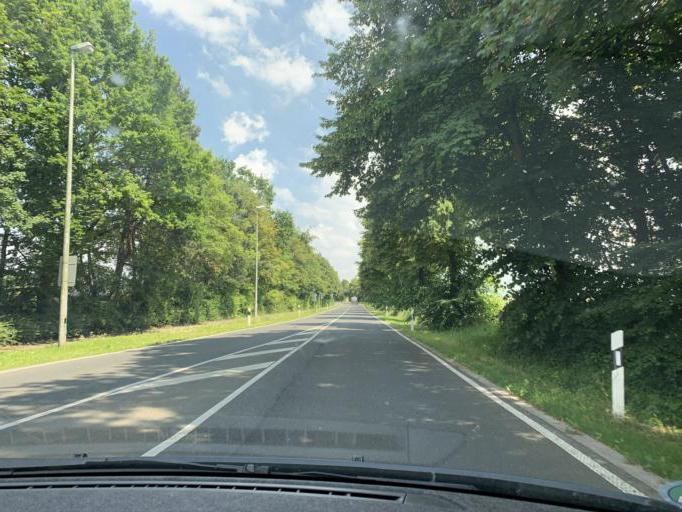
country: DE
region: North Rhine-Westphalia
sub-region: Regierungsbezirk Koln
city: Bedburg
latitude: 51.0346
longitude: 6.6167
